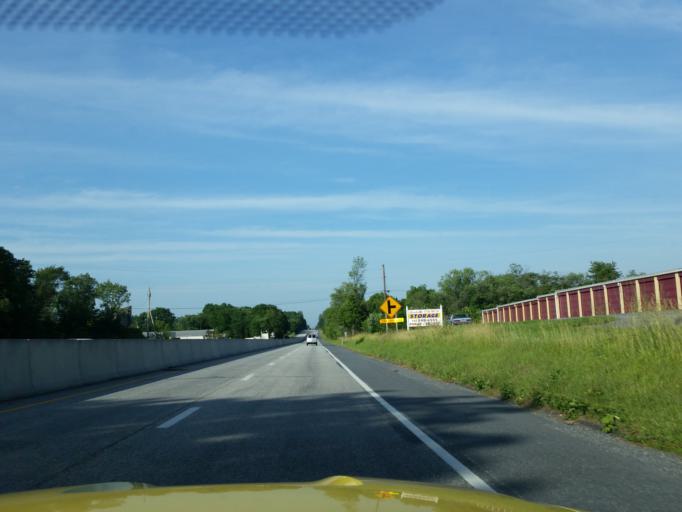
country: US
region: Pennsylvania
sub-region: Lebanon County
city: Palmyra
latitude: 40.3940
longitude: -76.6117
